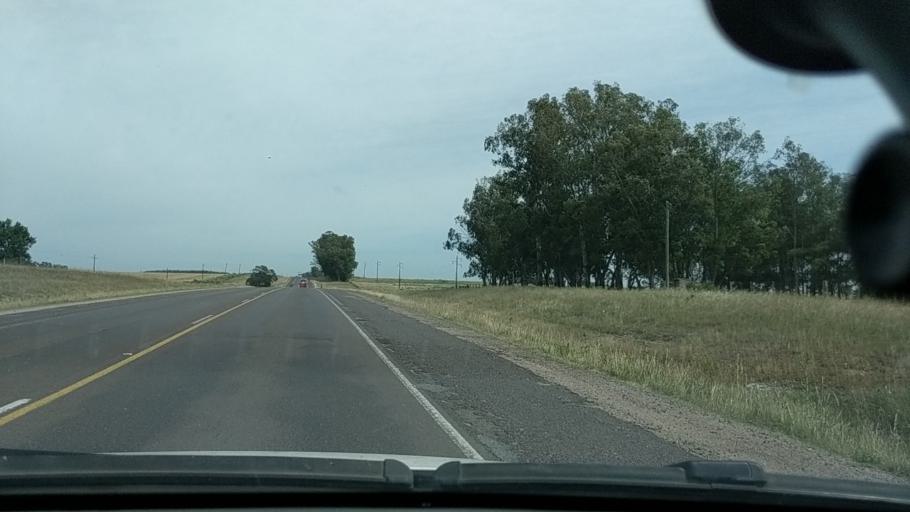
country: UY
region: Durazno
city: Durazno
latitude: -33.4869
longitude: -56.4375
